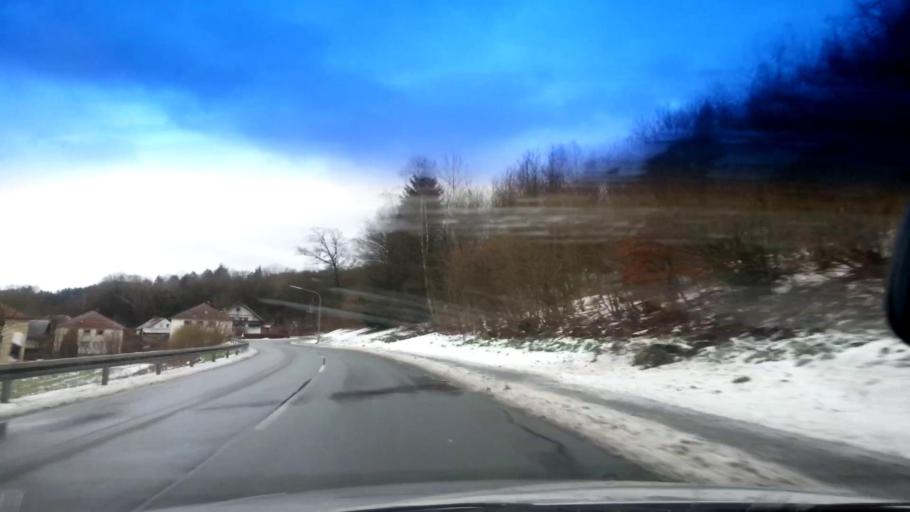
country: DE
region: Bavaria
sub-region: Upper Franconia
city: Gefrees
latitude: 50.0922
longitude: 11.7507
